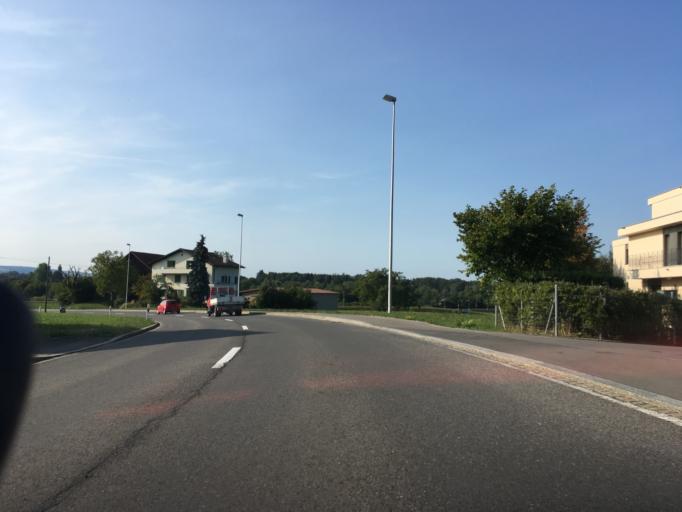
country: CH
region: Lucerne
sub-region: Lucerne-Land District
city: Meierskappel
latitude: 47.1435
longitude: 8.4526
